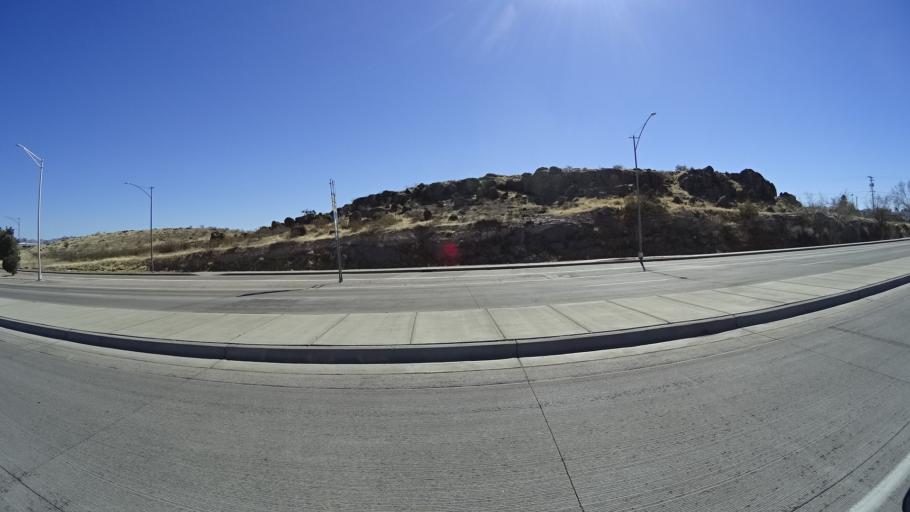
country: US
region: Arizona
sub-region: Mohave County
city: Kingman
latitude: 35.2157
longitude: -114.0126
